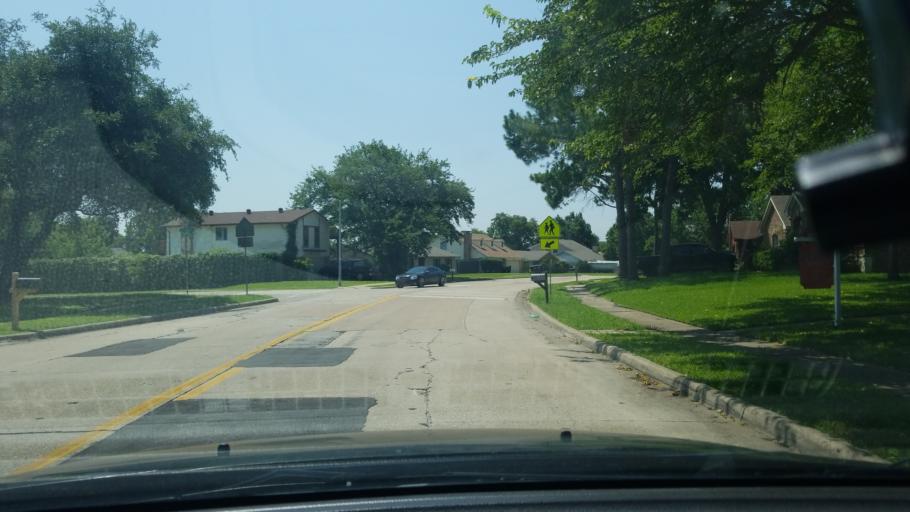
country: US
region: Texas
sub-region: Dallas County
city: Sunnyvale
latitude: 32.8279
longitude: -96.6110
